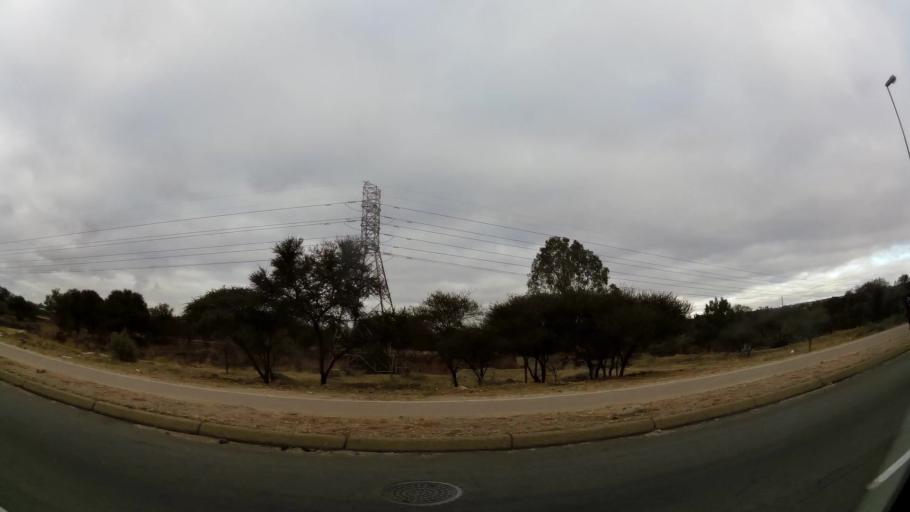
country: ZA
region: Limpopo
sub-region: Capricorn District Municipality
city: Polokwane
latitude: -23.8883
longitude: 29.4307
